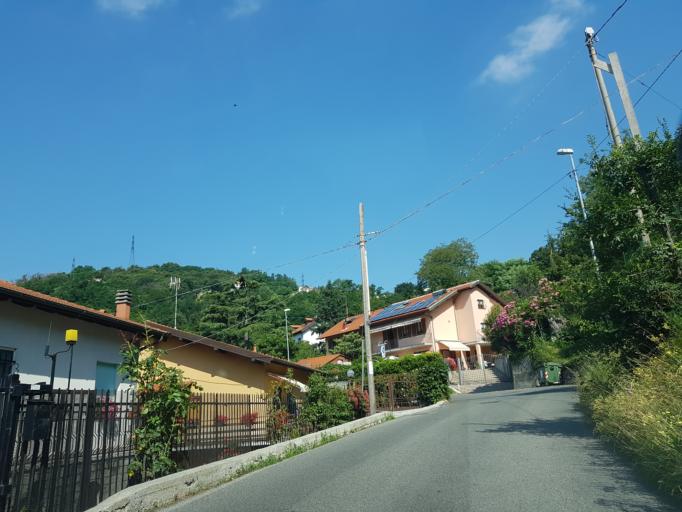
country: IT
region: Liguria
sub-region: Provincia di Genova
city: Pedemonte
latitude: 44.5034
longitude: 8.9232
